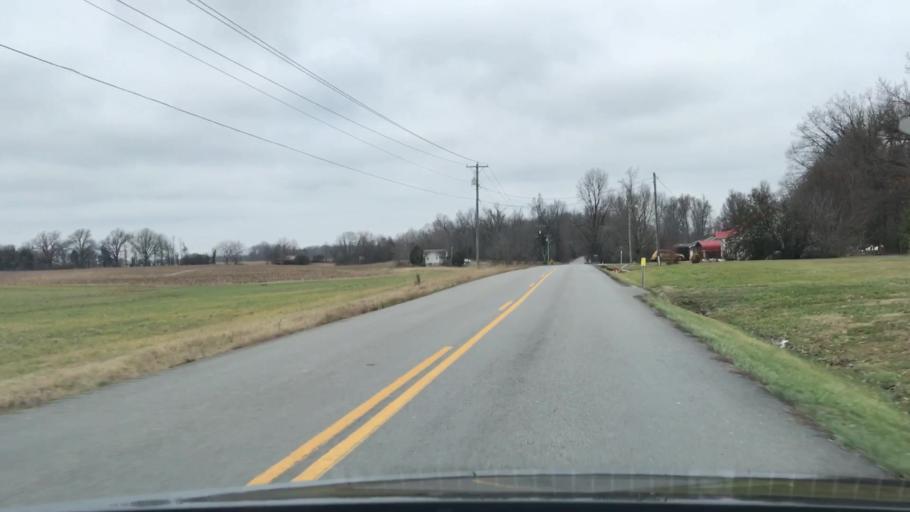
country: US
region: Kentucky
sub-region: Muhlenberg County
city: Morehead
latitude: 37.3598
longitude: -87.2321
